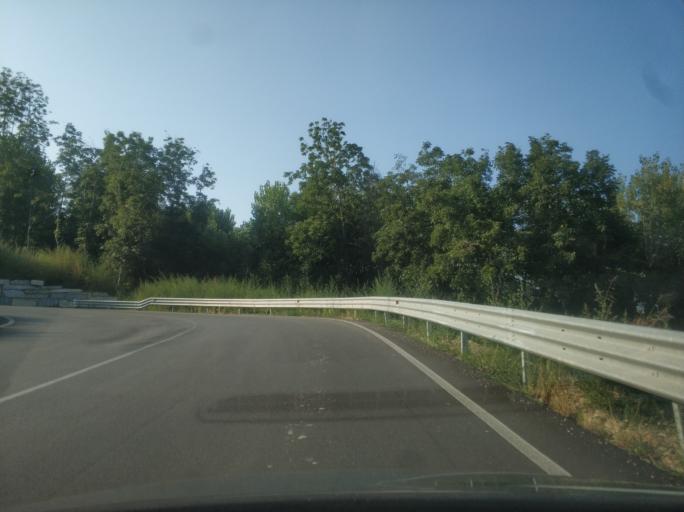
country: IT
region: Piedmont
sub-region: Provincia di Cuneo
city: Roreto
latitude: 44.6715
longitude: 7.8456
